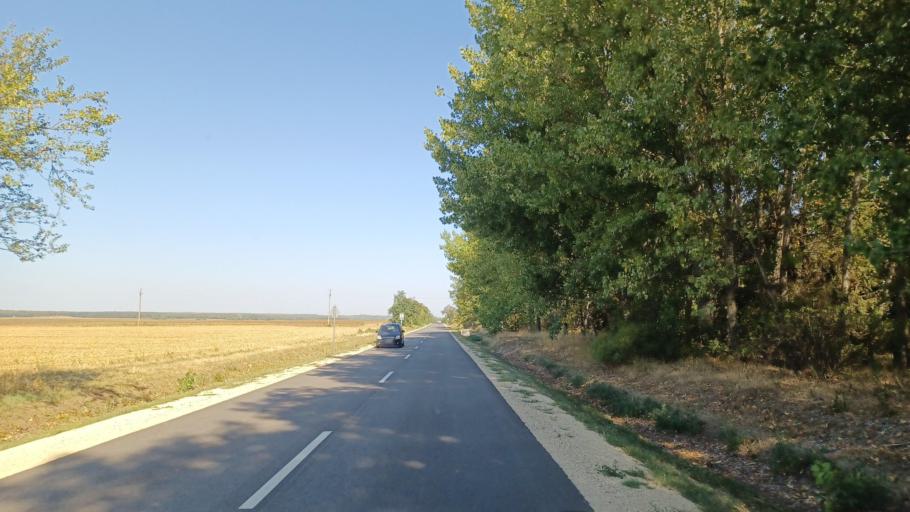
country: HU
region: Tolna
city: Paks
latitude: 46.6560
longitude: 18.8346
